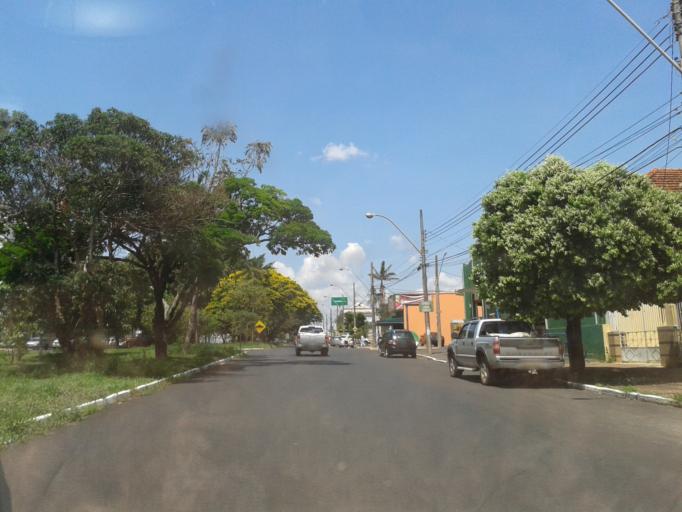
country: BR
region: Minas Gerais
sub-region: Araguari
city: Araguari
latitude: -18.6524
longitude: -48.1869
